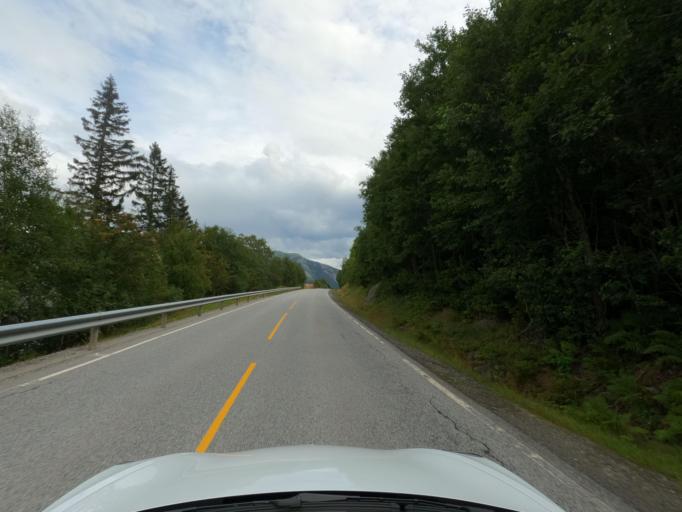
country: NO
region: Telemark
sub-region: Tinn
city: Rjukan
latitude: 59.9190
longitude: 8.8673
